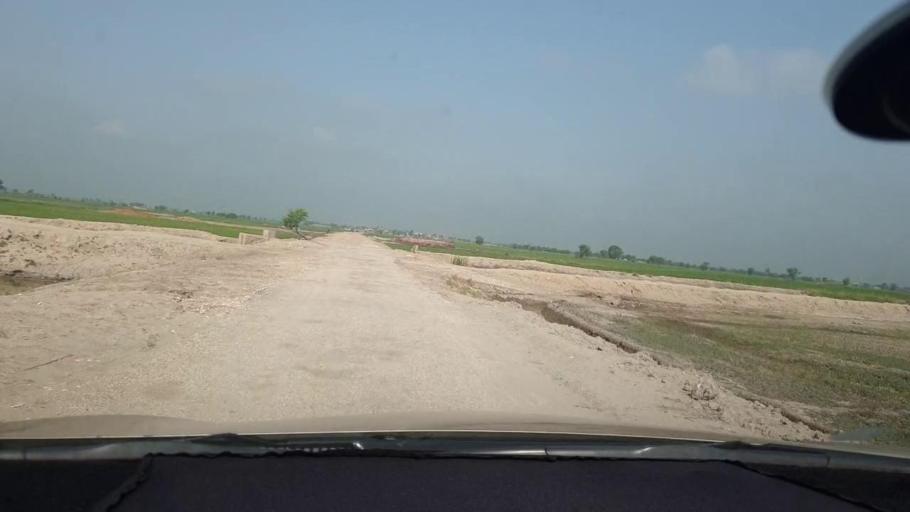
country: PK
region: Sindh
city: Kambar
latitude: 27.5370
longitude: 68.0586
